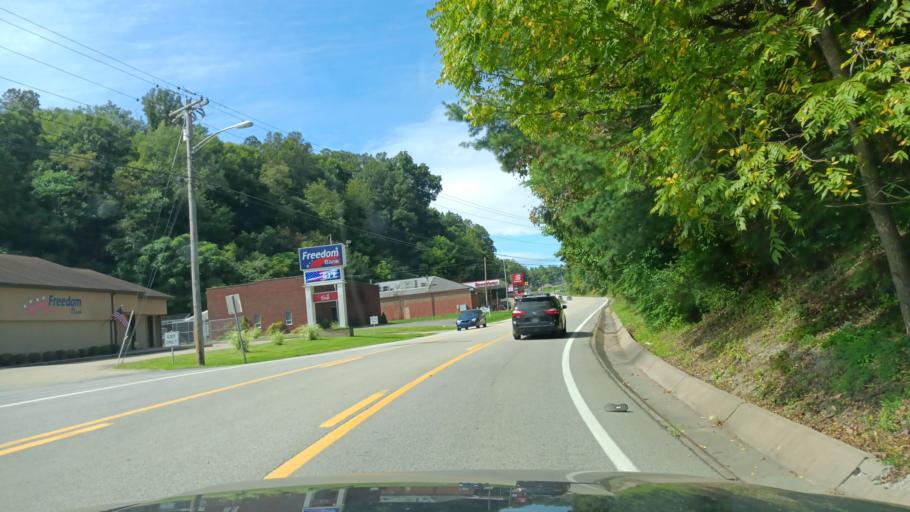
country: US
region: West Virginia
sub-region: Harrison County
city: Bridgeport
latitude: 39.2809
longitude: -80.2596
